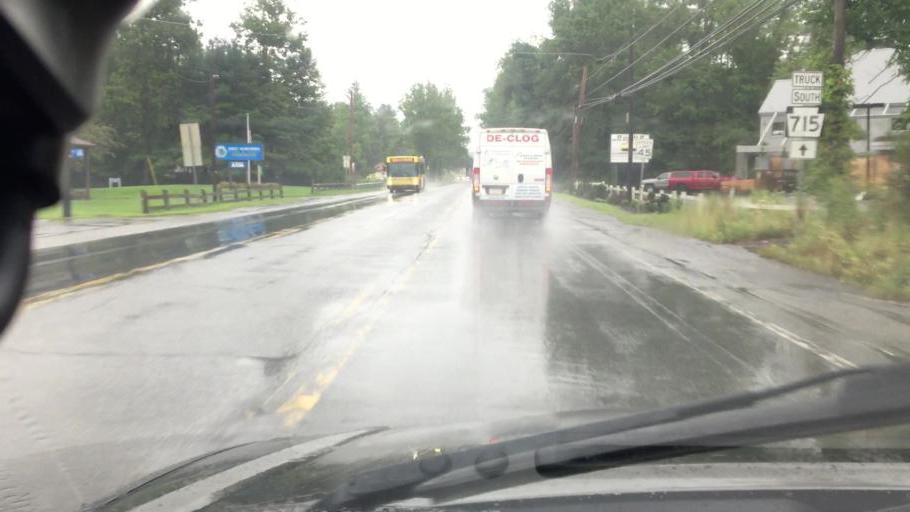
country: US
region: Pennsylvania
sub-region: Monroe County
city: Tannersville
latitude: 41.0306
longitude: -75.3011
